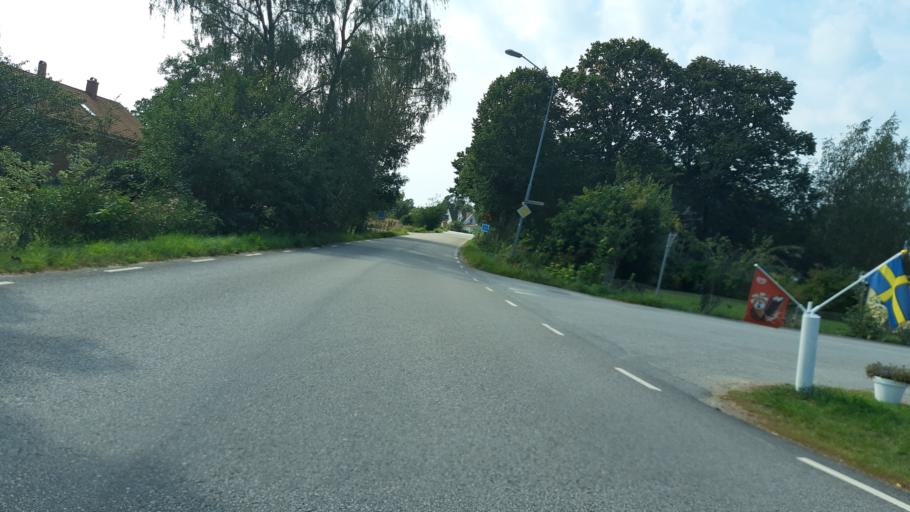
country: SE
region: Blekinge
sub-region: Karlskrona Kommun
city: Nattraby
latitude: 56.2274
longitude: 15.4214
